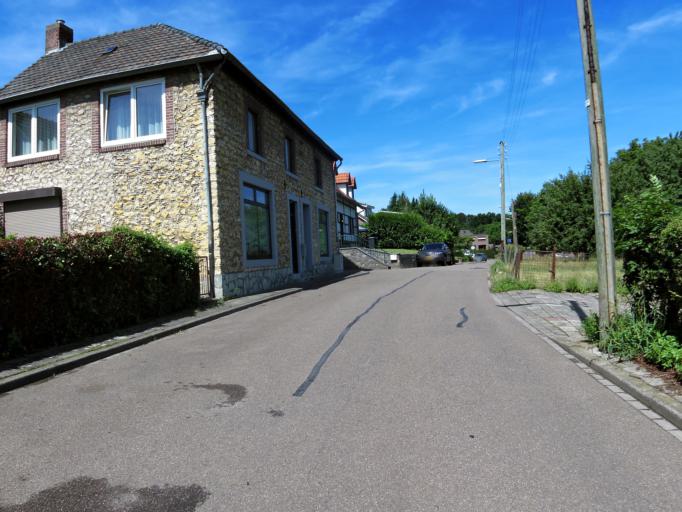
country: NL
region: Limburg
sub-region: Gemeente Heerlen
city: Heerlen
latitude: 50.8637
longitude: 5.9773
